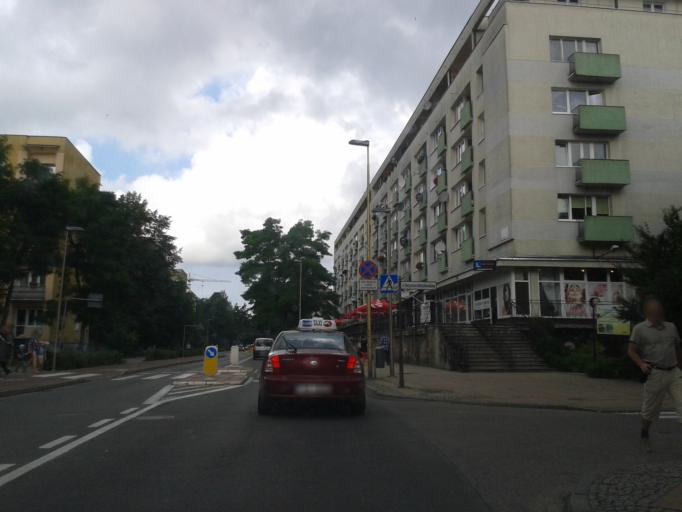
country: PL
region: West Pomeranian Voivodeship
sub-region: Swinoujscie
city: Swinoujscie
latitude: 53.9106
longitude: 14.2434
